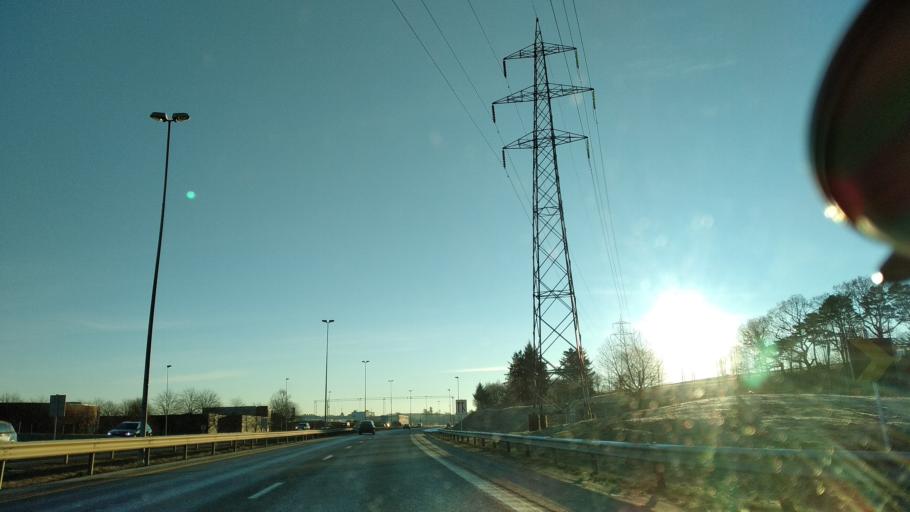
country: NO
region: Rogaland
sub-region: Sandnes
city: Sandnes
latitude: 58.8860
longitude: 5.7178
